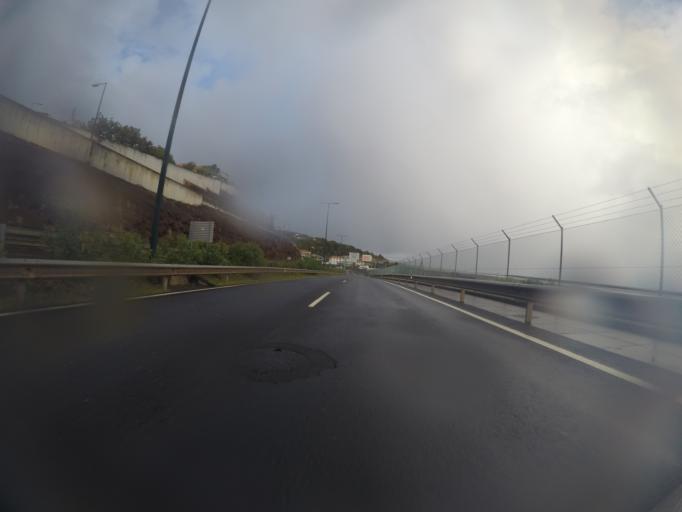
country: PT
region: Madeira
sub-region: Machico
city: Machico
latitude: 32.7048
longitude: -16.7685
